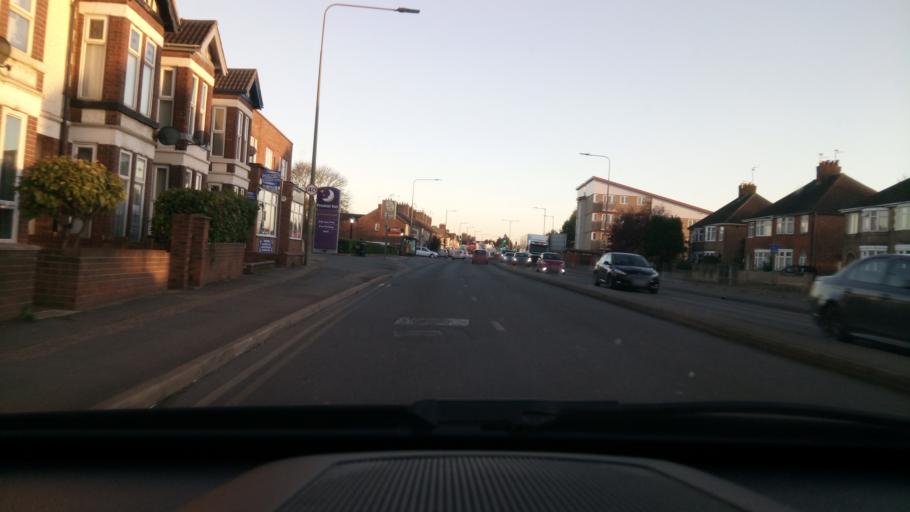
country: GB
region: England
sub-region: Peterborough
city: Peterborough
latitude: 52.6027
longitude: -0.2679
